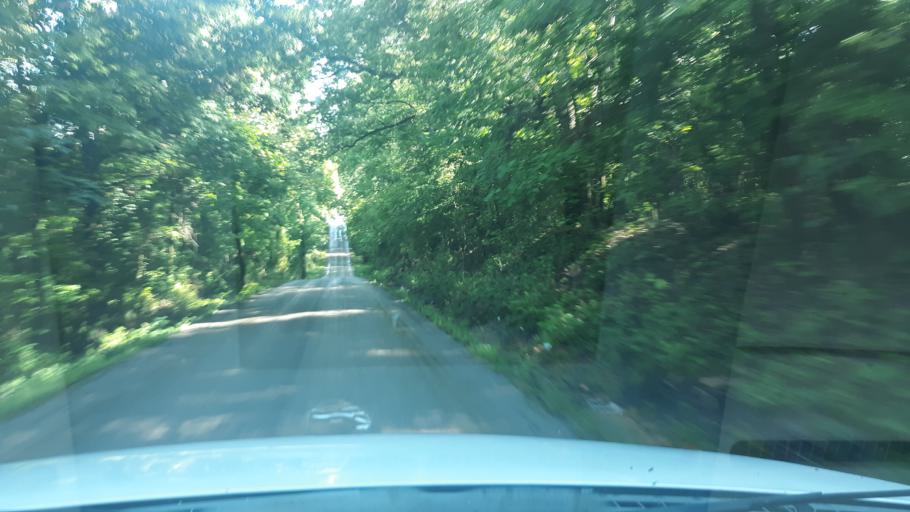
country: US
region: Illinois
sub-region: Saline County
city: Harrisburg
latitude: 37.8436
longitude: -88.5814
